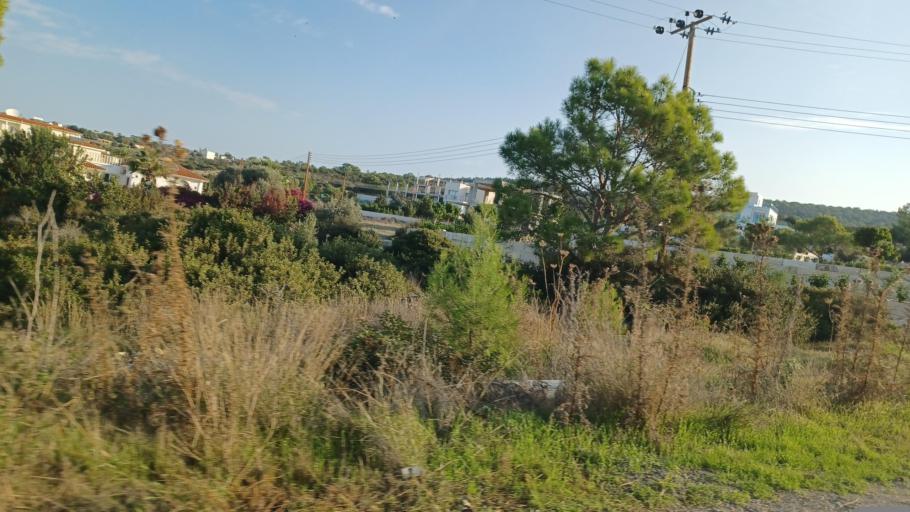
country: CY
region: Pafos
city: Pegeia
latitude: 34.8943
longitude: 32.3426
